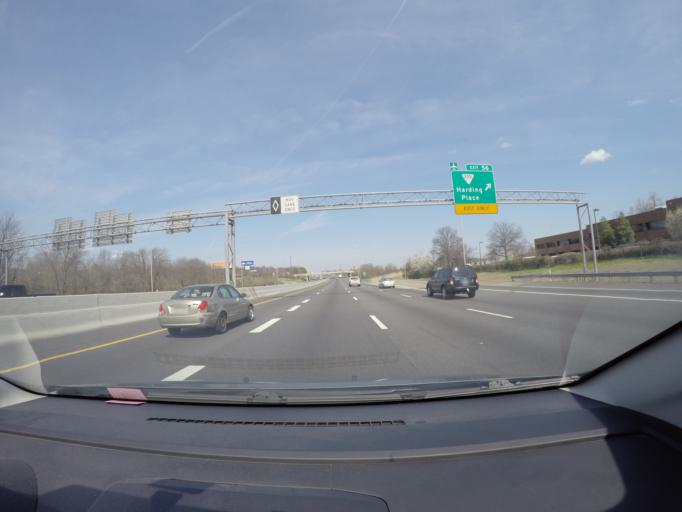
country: US
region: Tennessee
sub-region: Davidson County
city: Oak Hill
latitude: 36.0831
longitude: -86.6981
